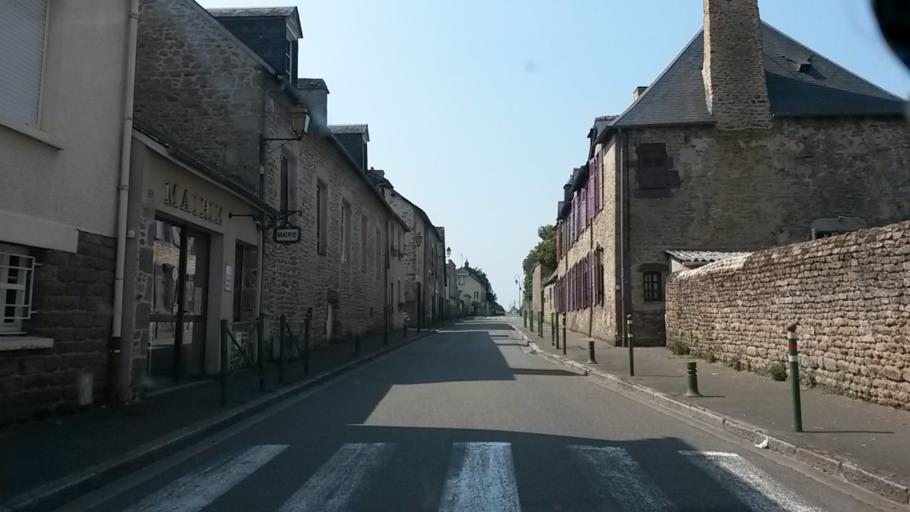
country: FR
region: Pays de la Loire
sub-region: Departement de la Mayenne
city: Saint-Pierre-des-Nids
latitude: 48.3986
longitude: -0.1009
